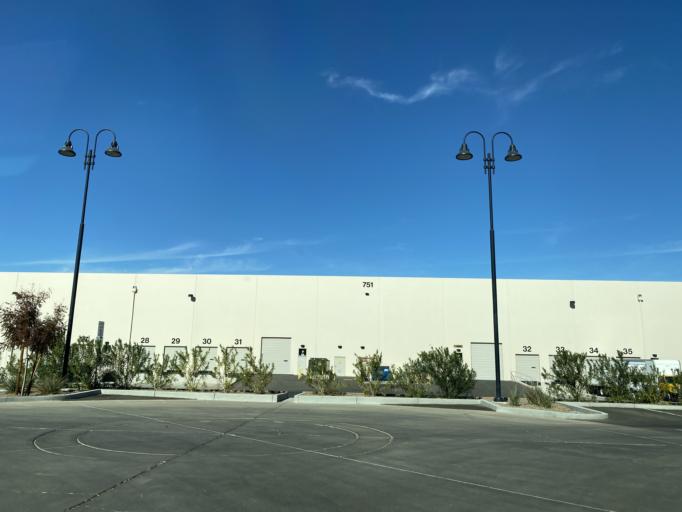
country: US
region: Nevada
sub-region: Clark County
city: Henderson
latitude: 36.0549
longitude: -115.0174
